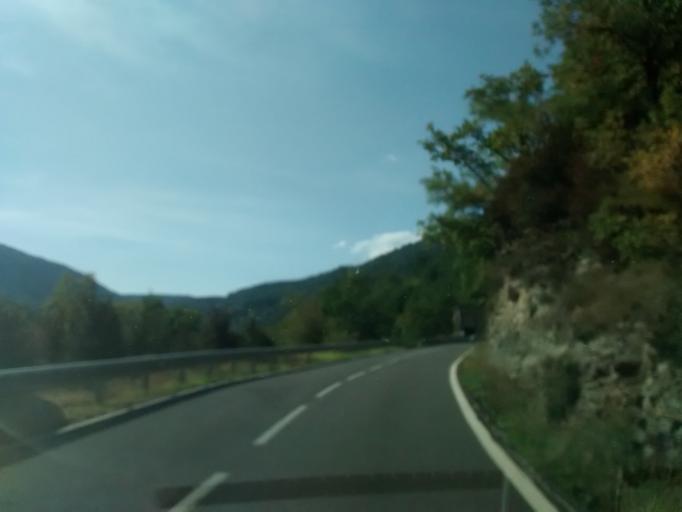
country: ES
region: Aragon
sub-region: Provincia de Huesca
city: Broto
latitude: 42.6121
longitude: -0.1234
